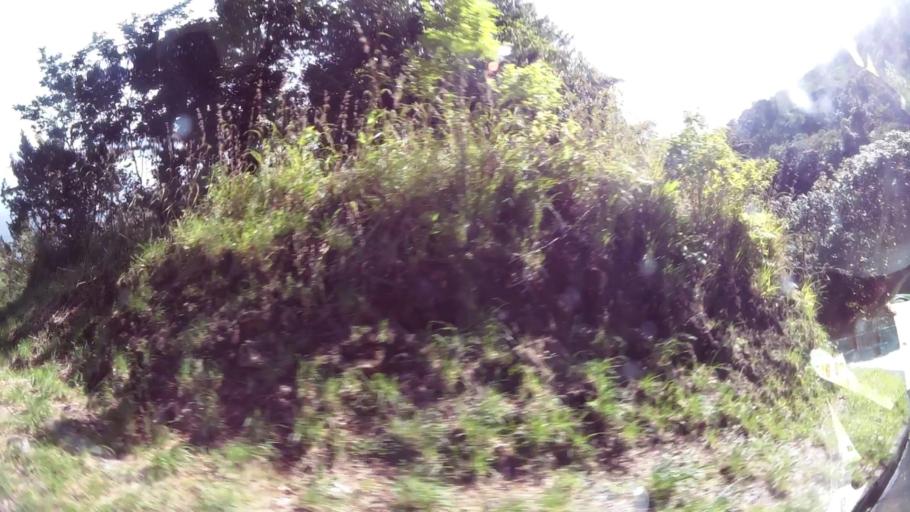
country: DM
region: Saint Paul
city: Pont Casse
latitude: 15.3732
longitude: -61.3460
